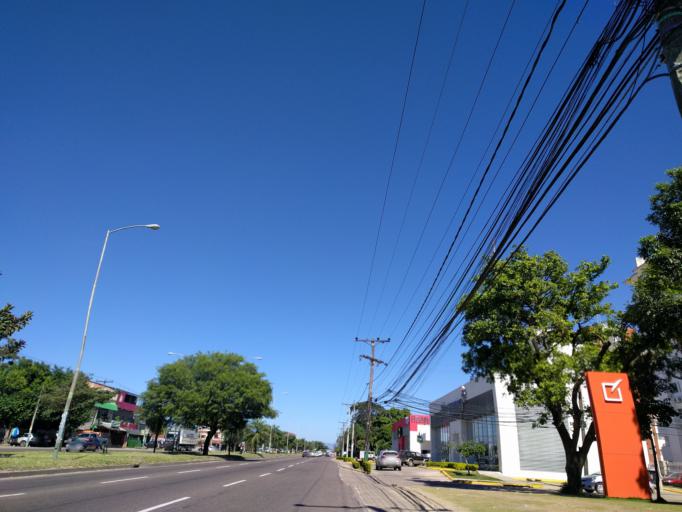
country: BO
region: Santa Cruz
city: Santa Cruz de la Sierra
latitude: -17.8199
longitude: -63.2175
